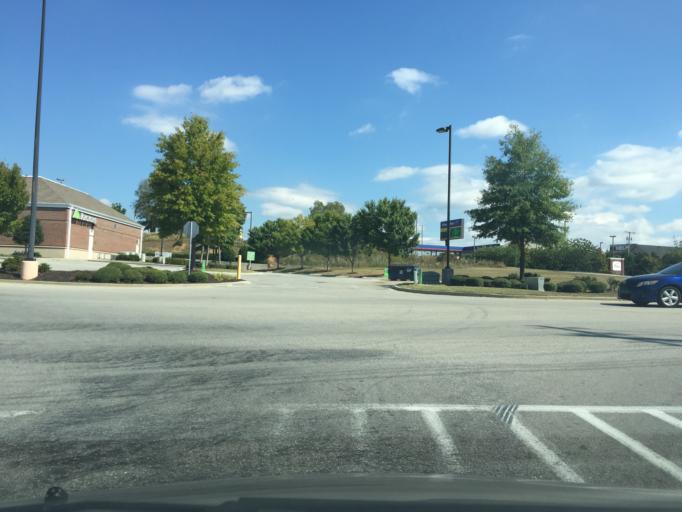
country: US
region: Tennessee
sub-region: Hamilton County
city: Collegedale
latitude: 35.0827
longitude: -85.0638
